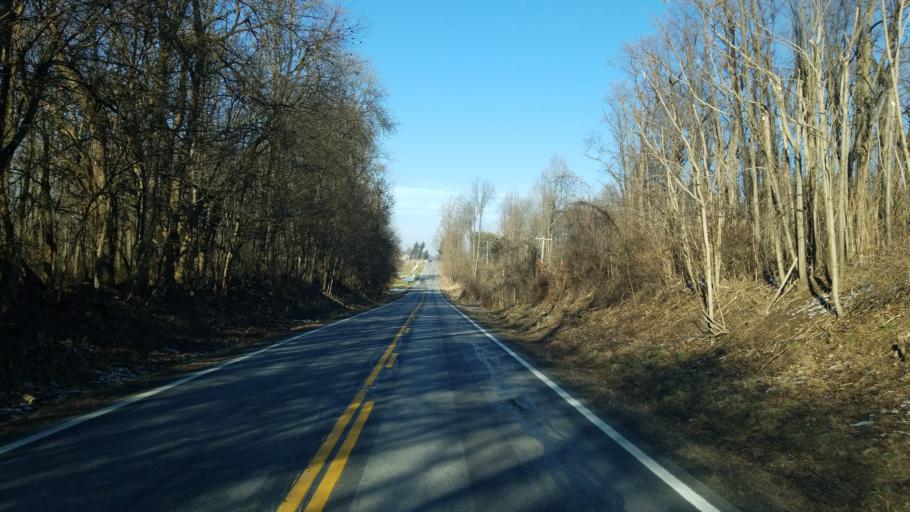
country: US
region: Ohio
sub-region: Huron County
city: Willard
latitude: 41.1122
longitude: -82.6609
